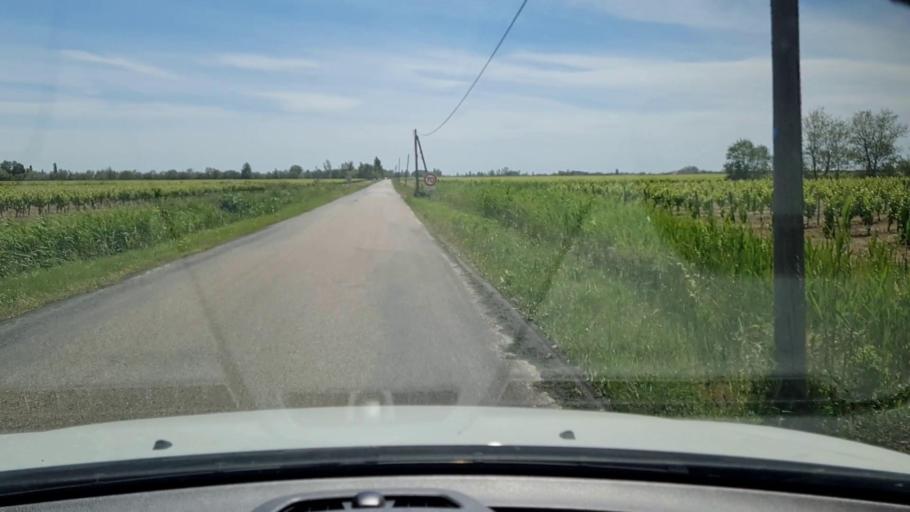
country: FR
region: Languedoc-Roussillon
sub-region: Departement du Gard
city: Vauvert
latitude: 43.5736
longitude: 4.3307
